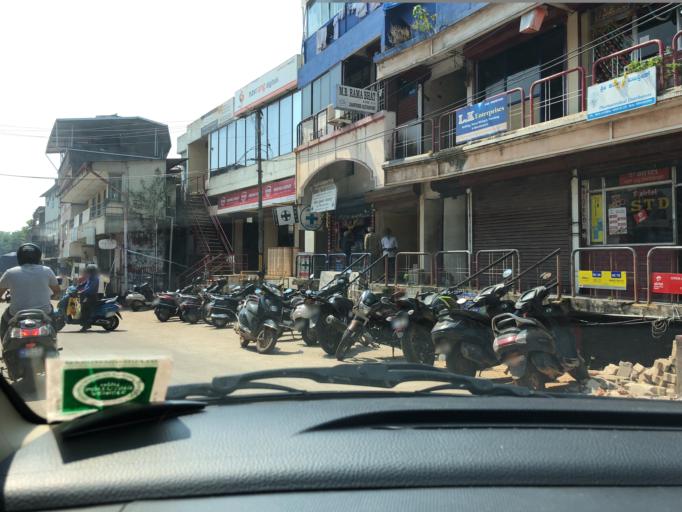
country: IN
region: Karnataka
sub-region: Dakshina Kannada
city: Ullal
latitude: 12.8618
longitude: 74.8336
